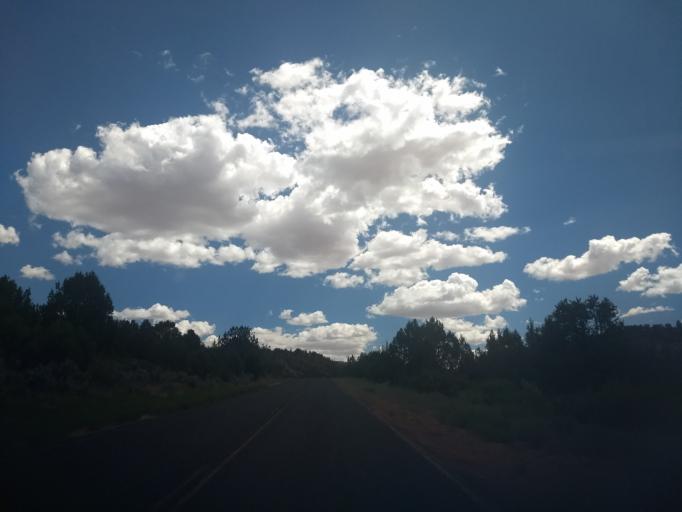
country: US
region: Utah
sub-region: Kane County
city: Kanab
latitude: 37.1163
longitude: -112.6773
